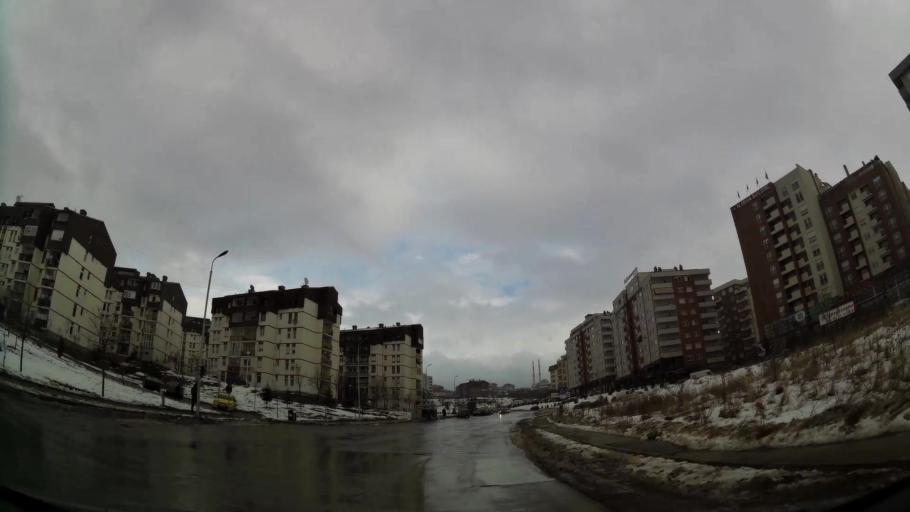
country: XK
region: Pristina
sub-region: Komuna e Prishtines
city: Pristina
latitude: 42.6560
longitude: 21.1794
